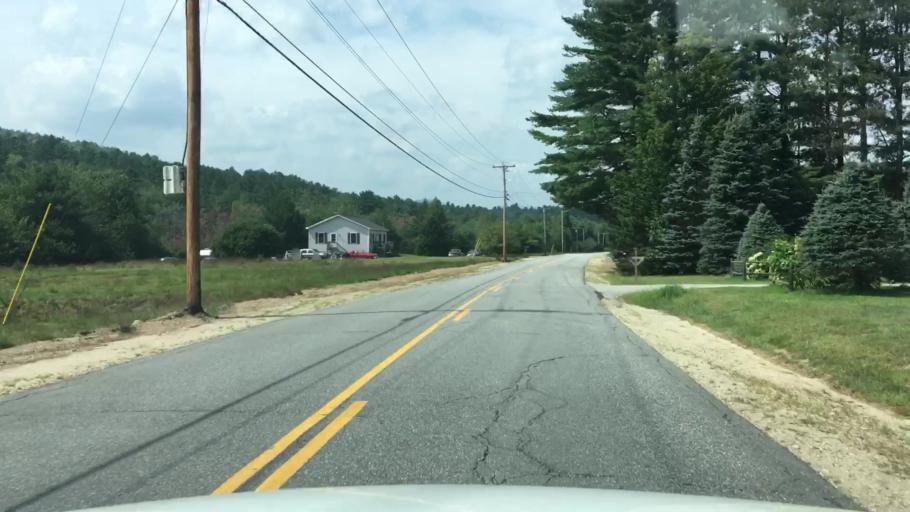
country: US
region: Maine
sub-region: Oxford County
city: Rumford
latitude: 44.5240
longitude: -70.6313
